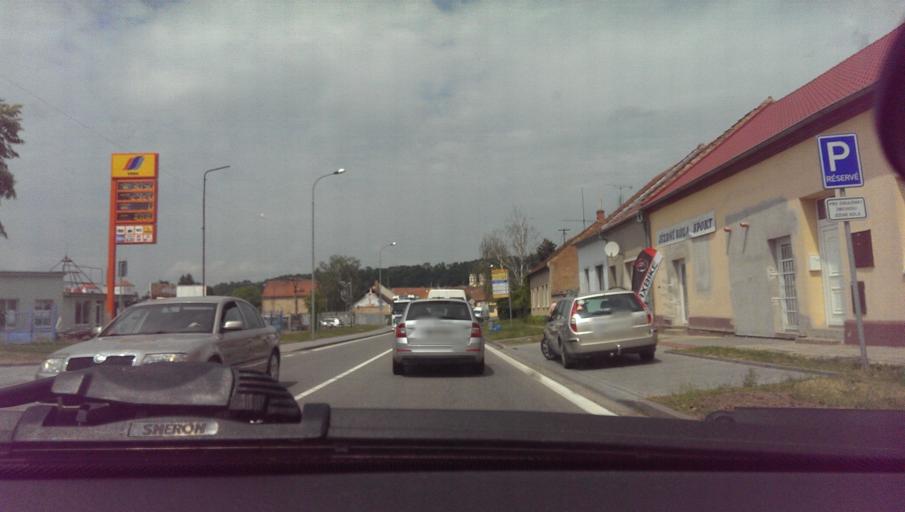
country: CZ
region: South Moravian
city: Bucovice
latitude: 49.1466
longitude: 17.0070
